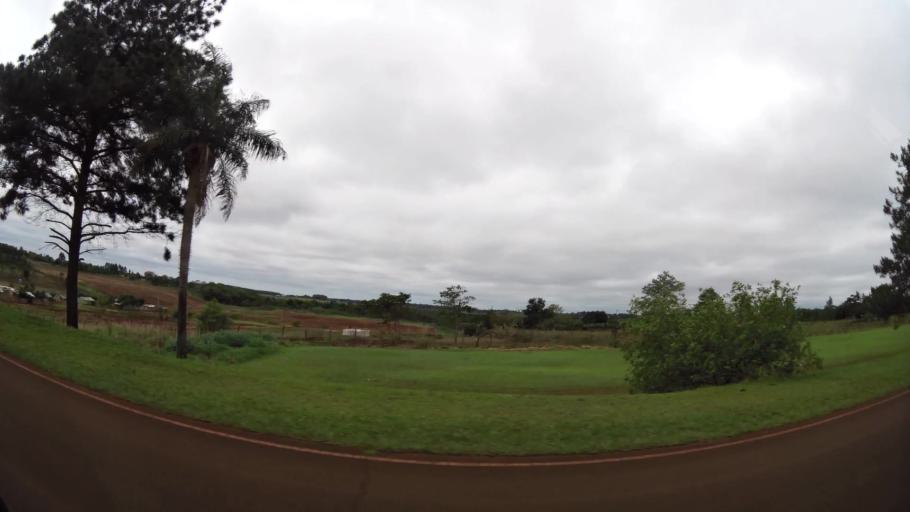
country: PY
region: Alto Parana
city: Colonia Yguazu
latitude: -25.4805
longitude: -54.8611
